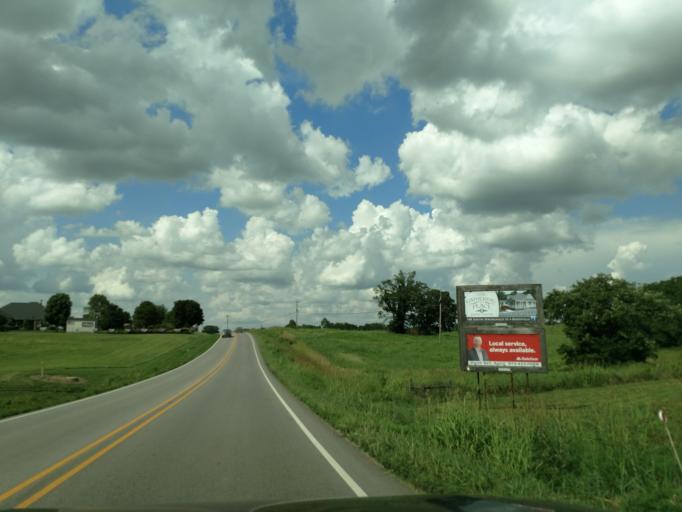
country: US
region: Arkansas
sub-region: Carroll County
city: Berryville
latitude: 36.3840
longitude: -93.5670
